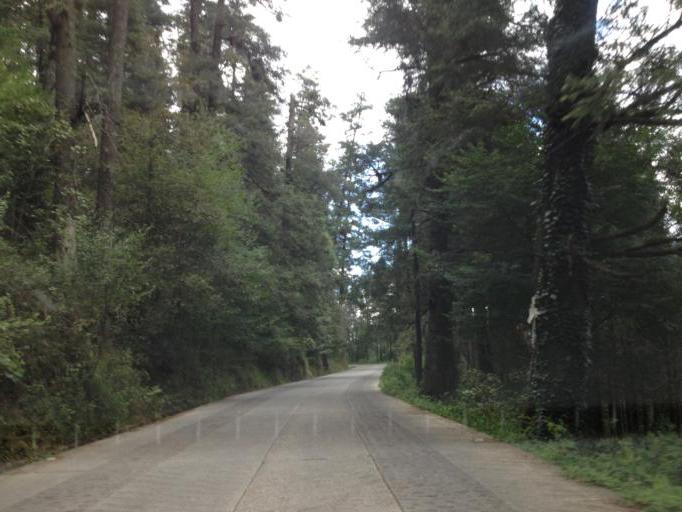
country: MX
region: Hidalgo
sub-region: Pachuca de Soto
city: San Miguel Cerezo (El Cerezo)
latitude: 20.2134
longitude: -98.7010
